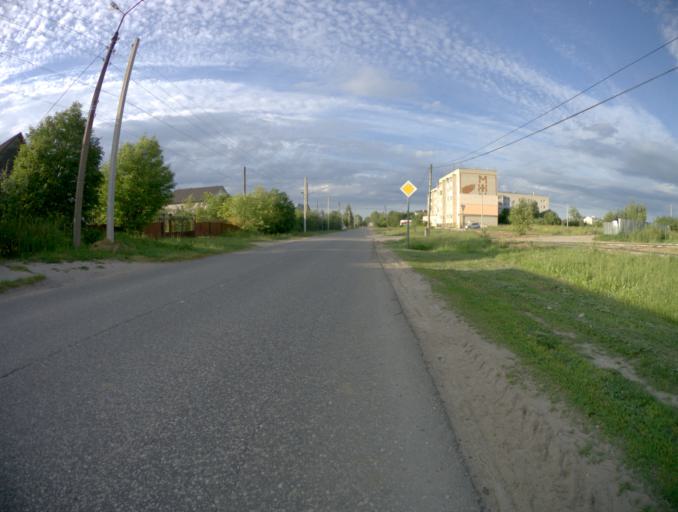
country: RU
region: Vladimir
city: Gorokhovets
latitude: 56.1938
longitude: 42.6612
